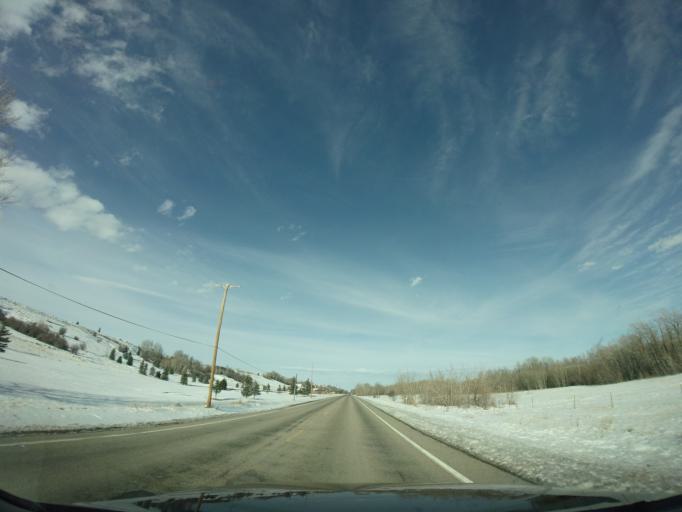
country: US
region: Montana
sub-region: Carbon County
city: Red Lodge
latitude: 45.2079
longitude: -109.2440
